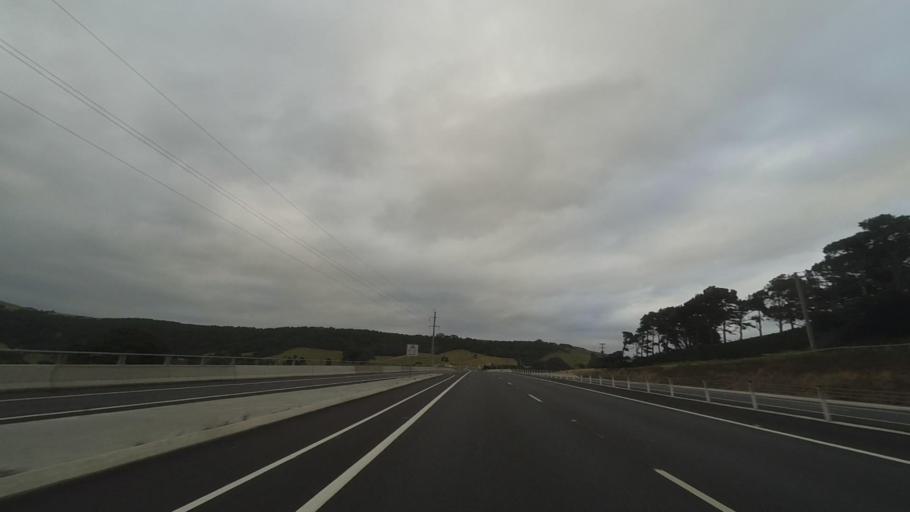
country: AU
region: New South Wales
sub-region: Kiama
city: Gerringong
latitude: -34.7197
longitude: 150.8308
